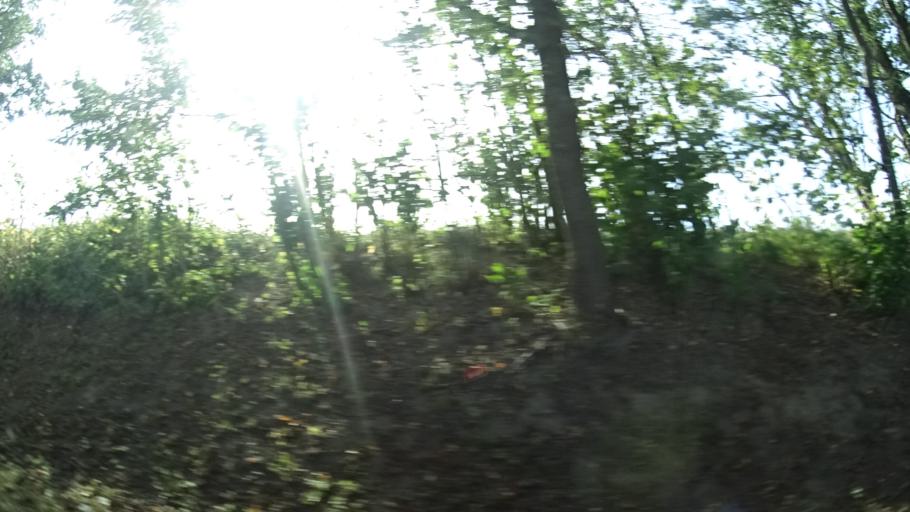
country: DE
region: Thuringia
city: Oberkatz
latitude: 50.5586
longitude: 10.2261
